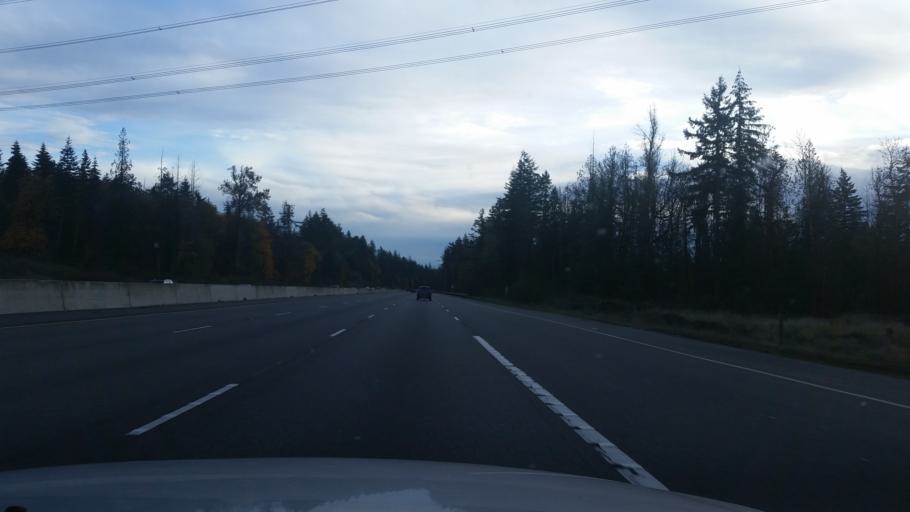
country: US
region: Washington
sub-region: Thurston County
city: Grand Mound
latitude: 46.8670
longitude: -122.9705
